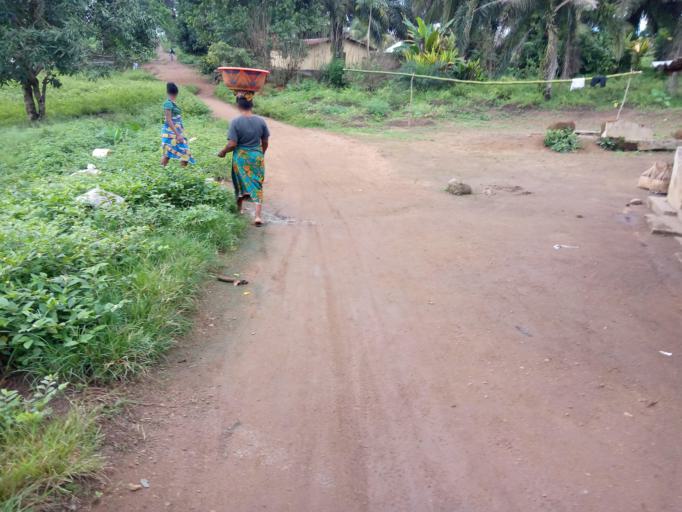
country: SL
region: Eastern Province
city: Buedu
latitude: 8.4565
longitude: -10.3342
